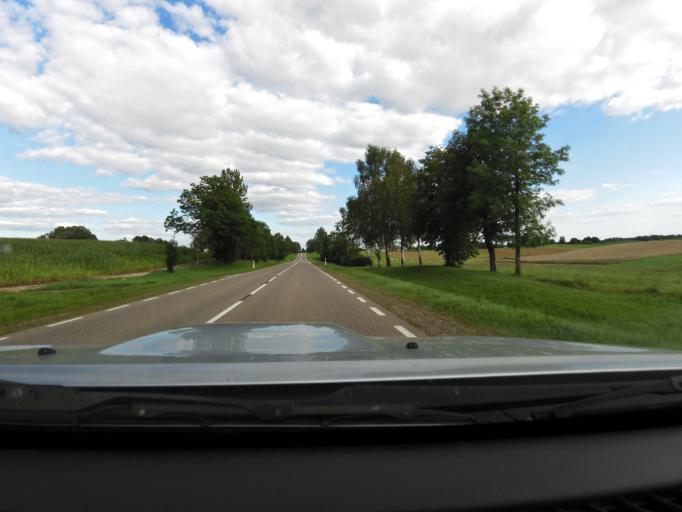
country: PL
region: Podlasie
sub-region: Powiat suwalski
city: Raczki
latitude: 53.8528
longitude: 22.7741
